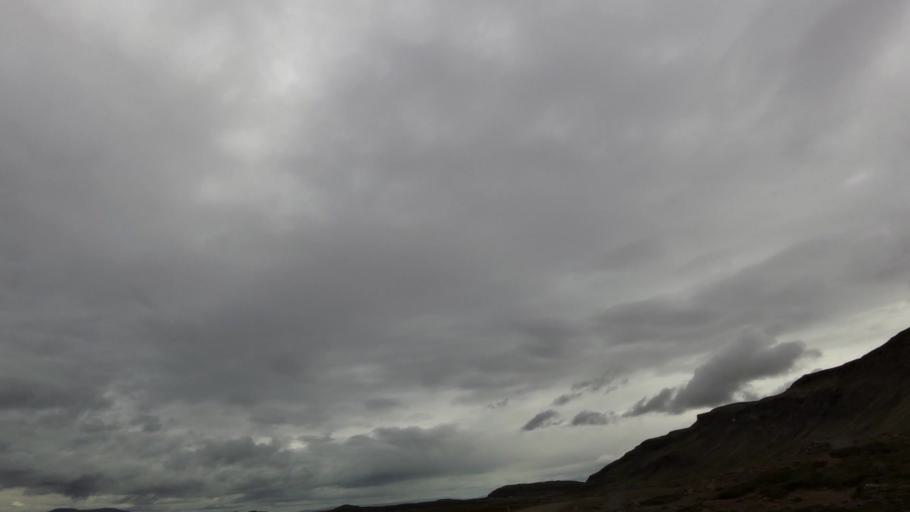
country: IS
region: West
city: Stykkisholmur
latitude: 65.0385
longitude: -22.4648
